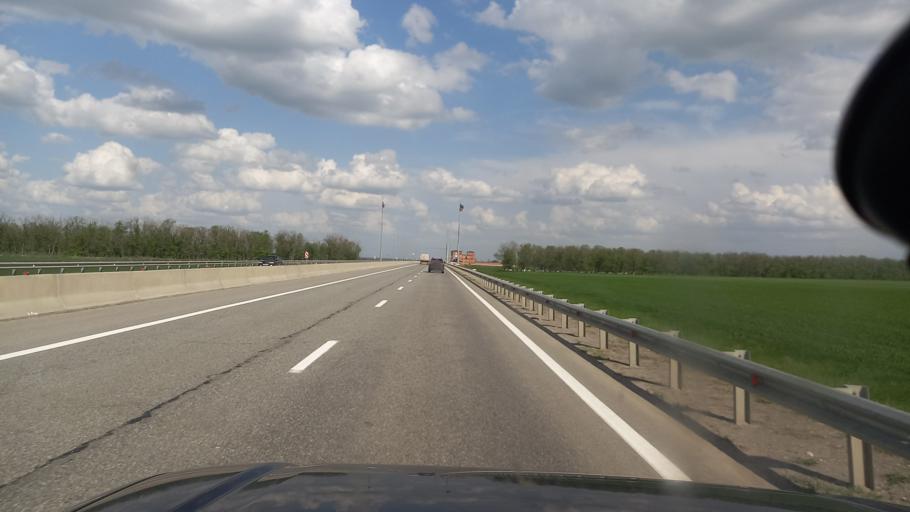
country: RU
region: Ingushetiya
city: Sernovodsk
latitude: 43.2791
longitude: 45.1038
